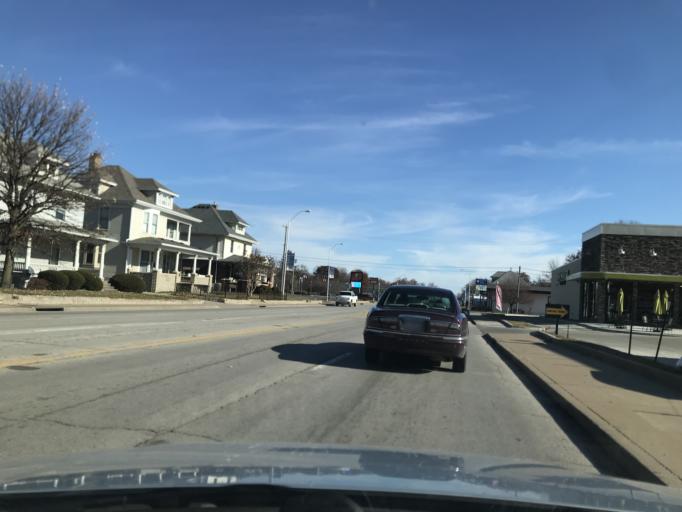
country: US
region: Illinois
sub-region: McDonough County
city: Macomb
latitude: 40.4586
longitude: -90.6670
